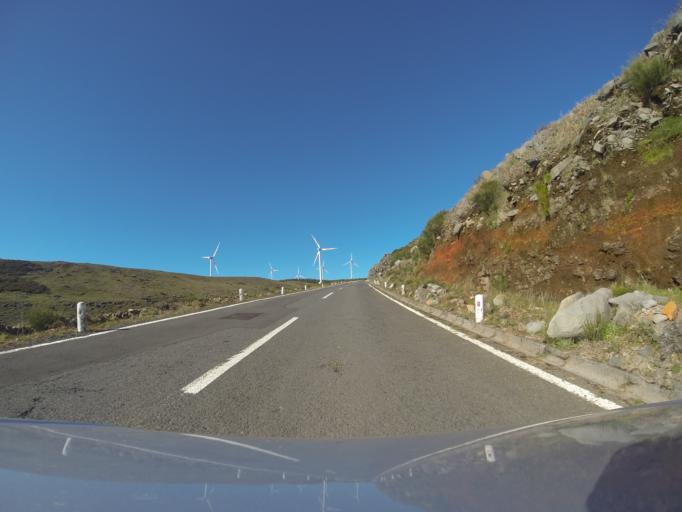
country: PT
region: Madeira
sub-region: Sao Vicente
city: Sao Vicente
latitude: 32.7393
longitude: -17.0598
